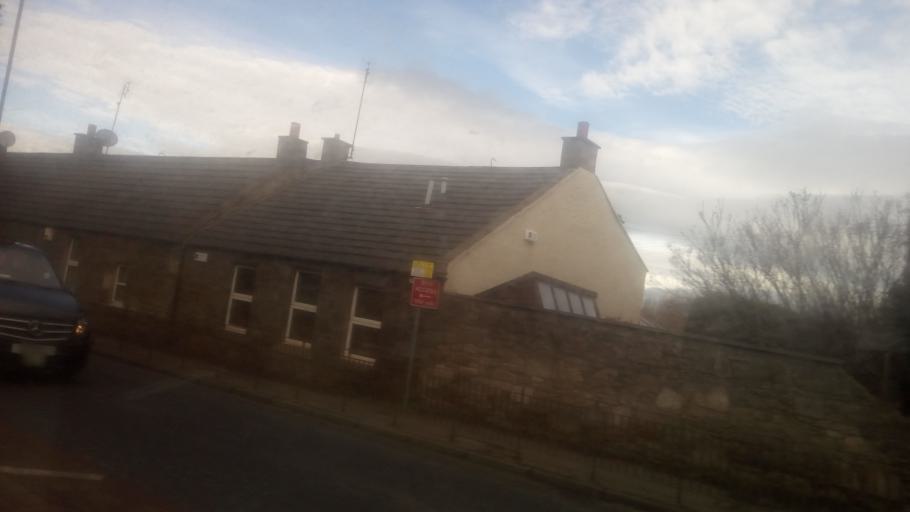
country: GB
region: Scotland
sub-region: Midlothian
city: Loanhead
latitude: 55.9182
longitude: -3.1348
